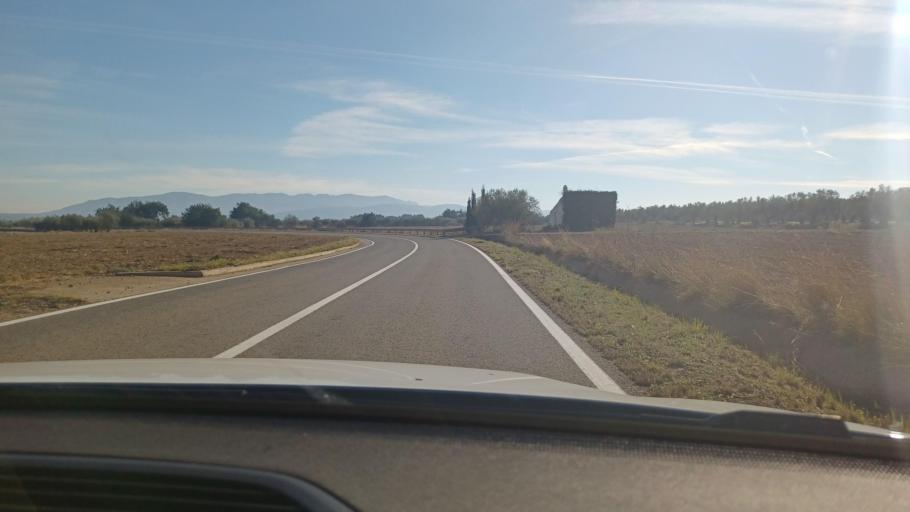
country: ES
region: Catalonia
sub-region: Provincia de Tarragona
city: Santa Barbara
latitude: 40.7206
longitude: 0.4468
